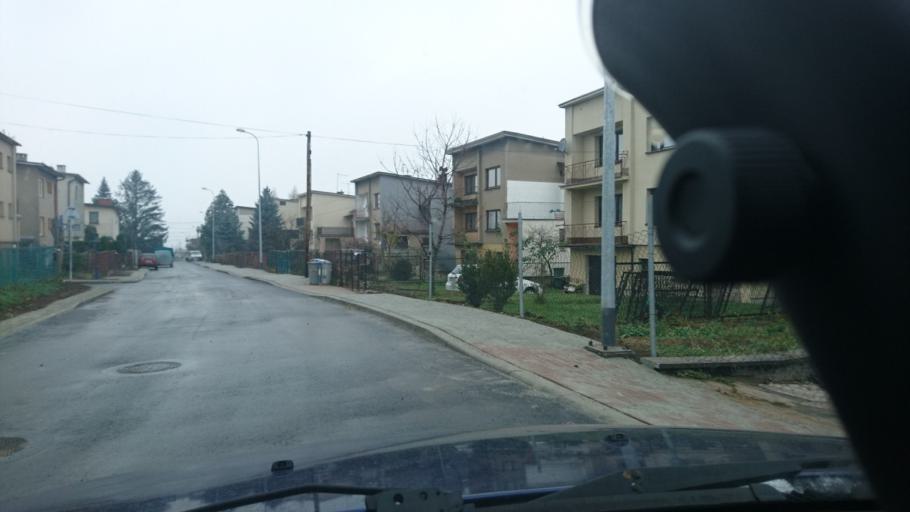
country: PL
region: Silesian Voivodeship
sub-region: Bielsko-Biala
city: Bielsko-Biala
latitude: 49.7972
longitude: 19.0721
